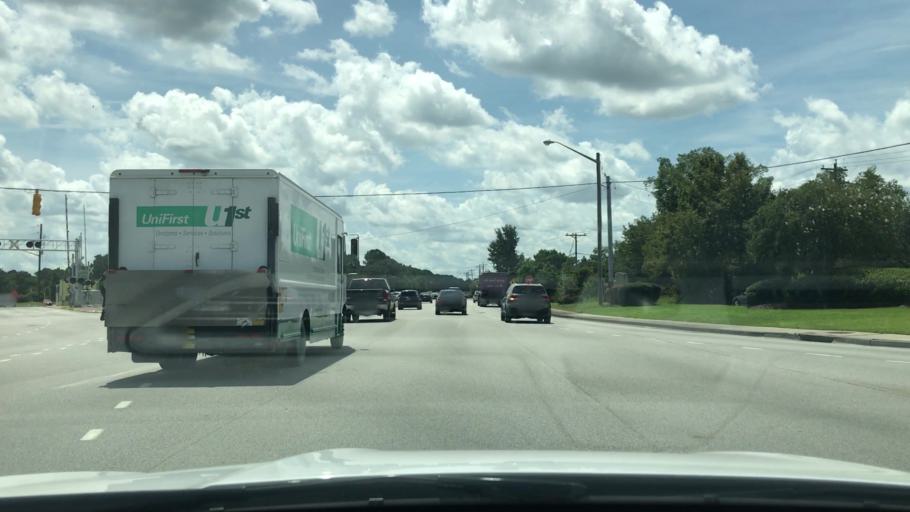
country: US
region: South Carolina
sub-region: Berkeley County
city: Goose Creek
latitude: 32.9963
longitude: -80.0388
